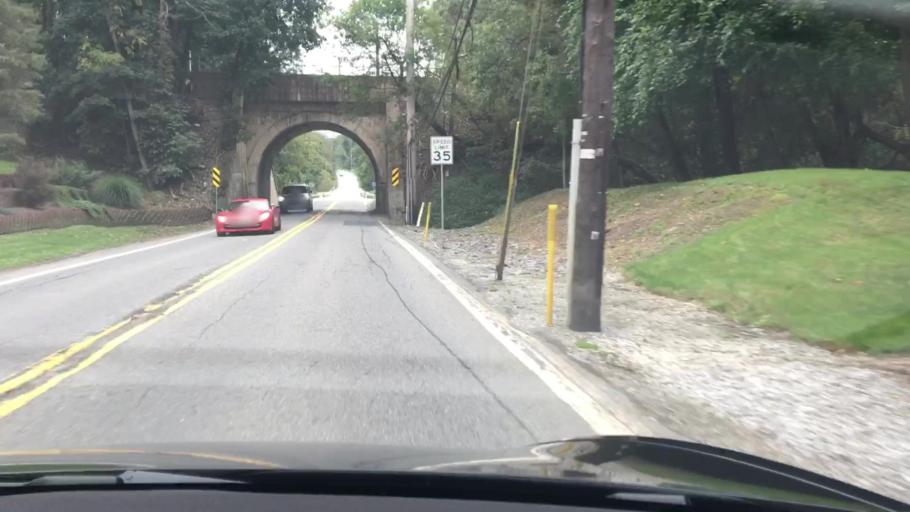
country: US
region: Pennsylvania
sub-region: Cumberland County
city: Mechanicsburg
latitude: 40.1660
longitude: -76.9779
